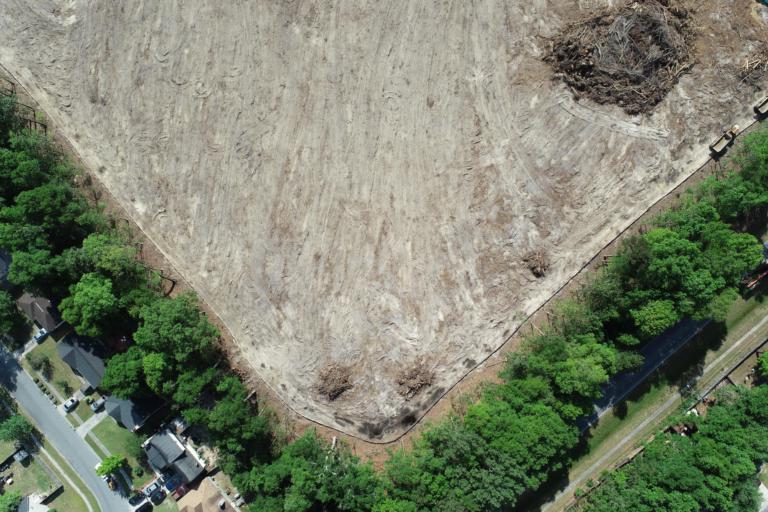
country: US
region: Georgia
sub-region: Chatham County
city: Georgetown
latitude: 32.0265
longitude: -81.2479
